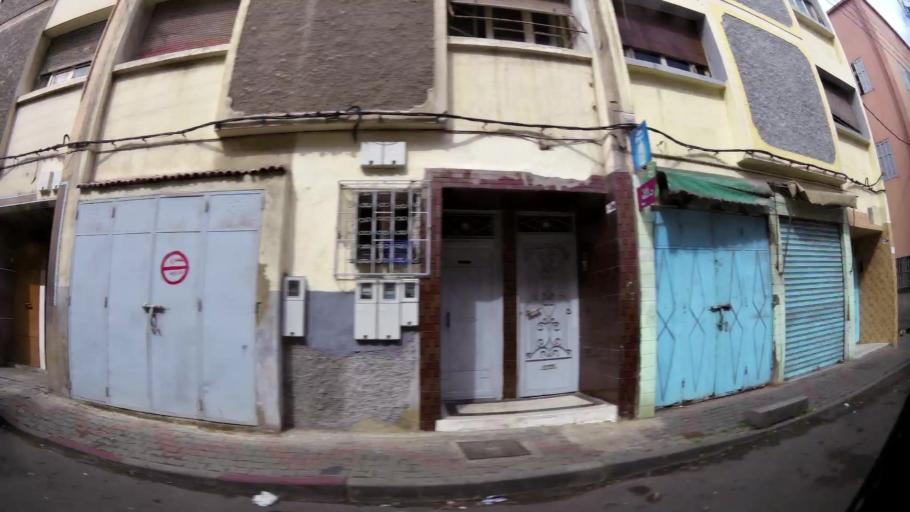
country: MA
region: Grand Casablanca
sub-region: Casablanca
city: Casablanca
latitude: 33.5845
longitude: -7.5751
